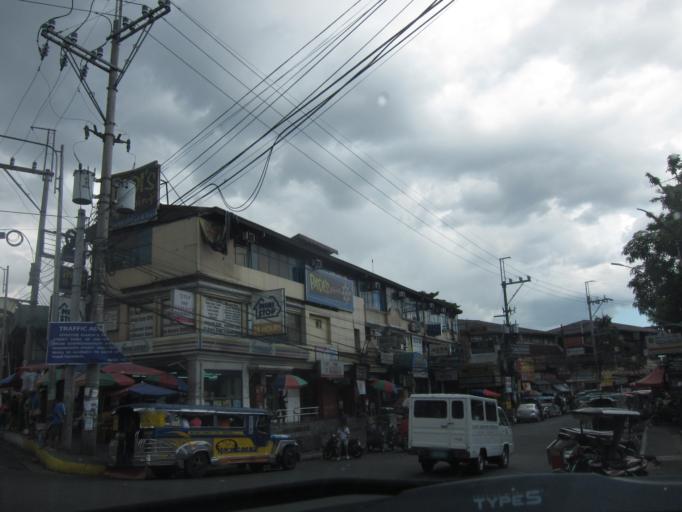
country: PH
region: Metro Manila
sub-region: Quezon City
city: Quezon City
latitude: 14.6533
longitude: 121.0525
